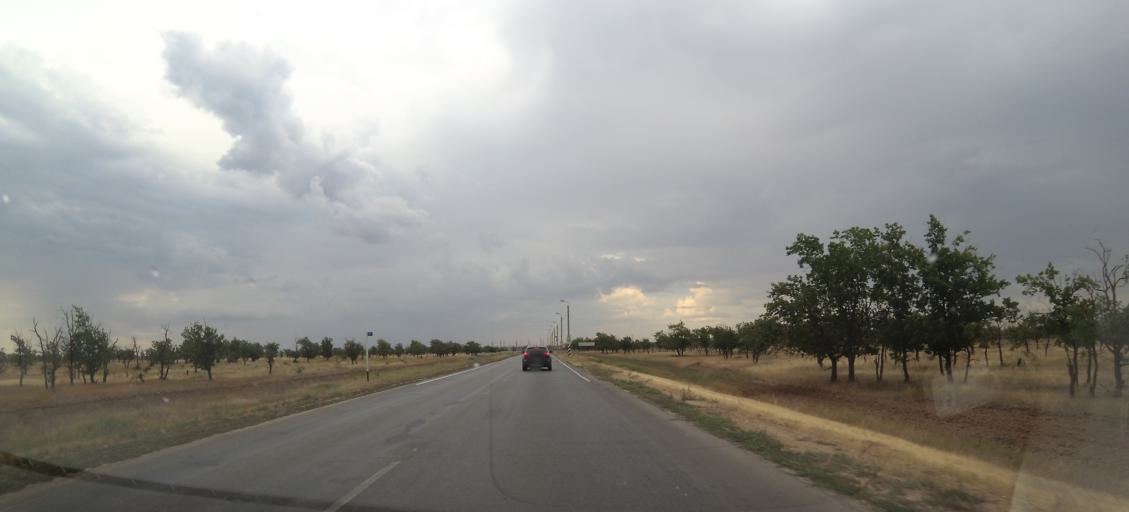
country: RU
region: Volgograd
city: Kotel'nikovo
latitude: 47.6130
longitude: 43.1206
